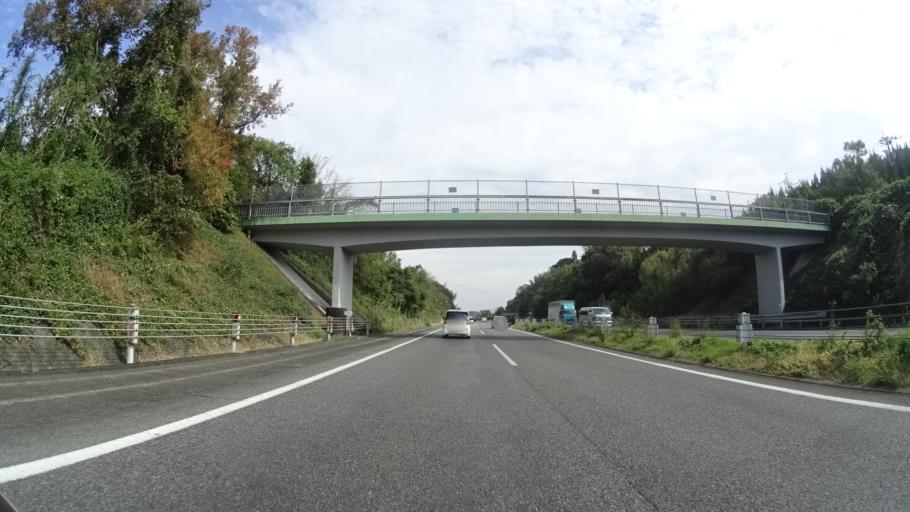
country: JP
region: Kumamoto
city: Yatsushiro
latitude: 32.5396
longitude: 130.6758
